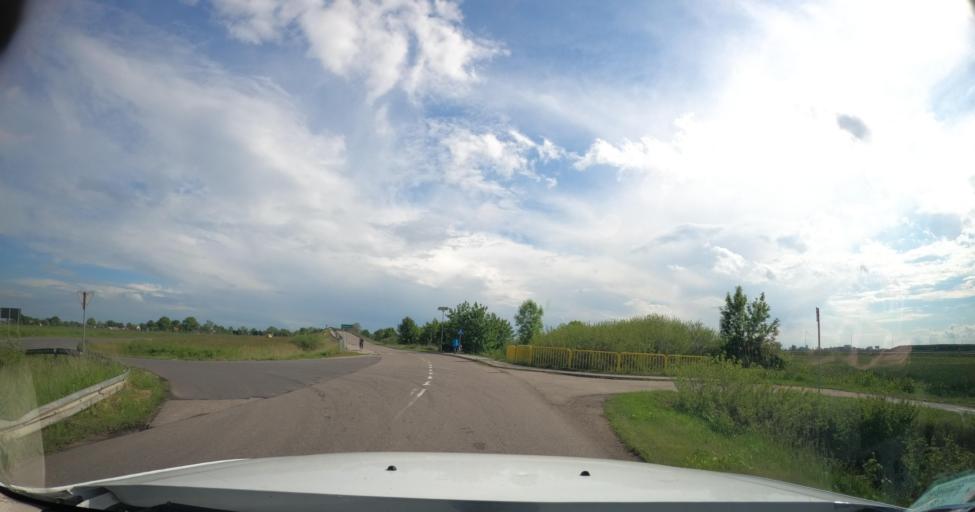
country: PL
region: Pomeranian Voivodeship
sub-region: Powiat nowodworski
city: Nowy Dwor Gdanski
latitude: 54.1968
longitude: 19.1399
